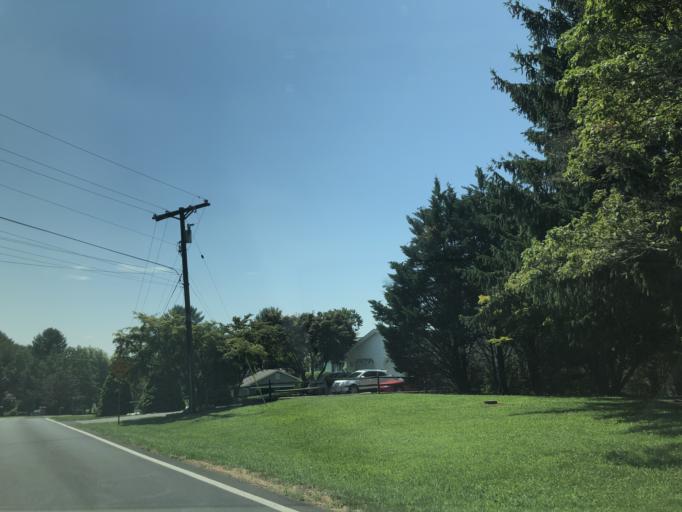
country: US
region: Maryland
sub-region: Carroll County
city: Eldersburg
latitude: 39.4423
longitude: -76.9567
